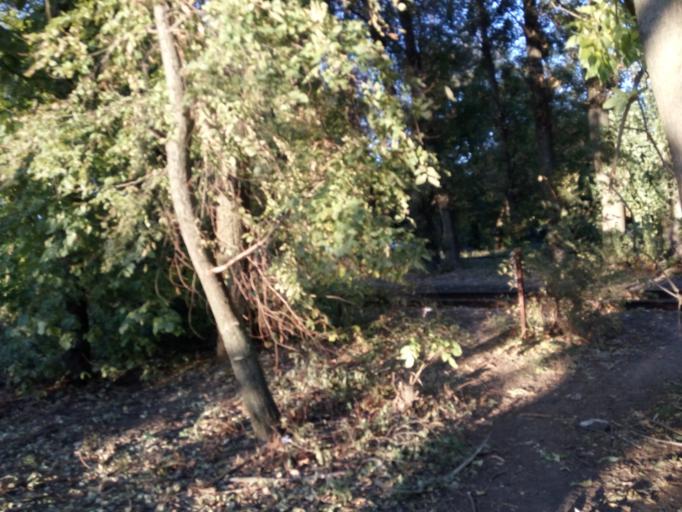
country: RU
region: Rostov
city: Rostov-na-Donu
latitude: 47.2450
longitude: 39.7562
